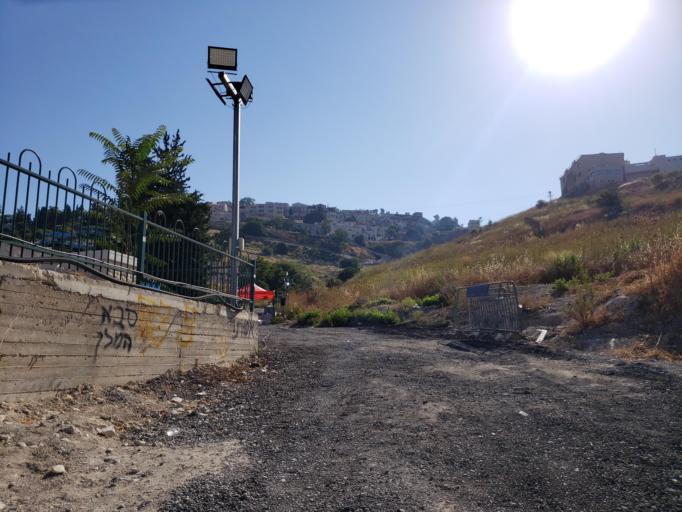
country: IL
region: Northern District
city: Safed
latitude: 32.9669
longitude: 35.4873
